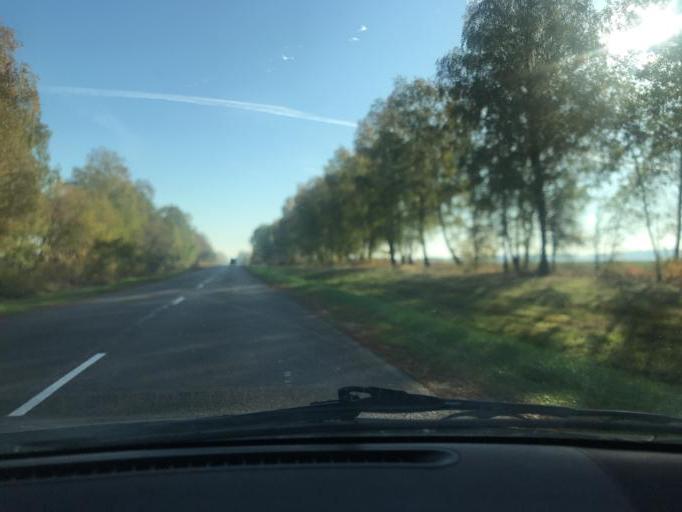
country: BY
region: Brest
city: Ivanava
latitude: 52.1452
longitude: 25.4793
